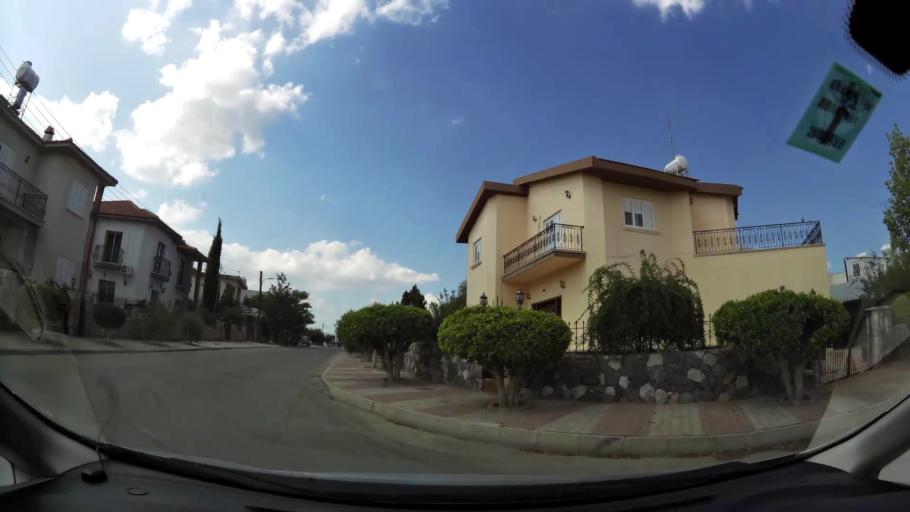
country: CY
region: Lefkosia
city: Nicosia
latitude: 35.2250
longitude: 33.2915
